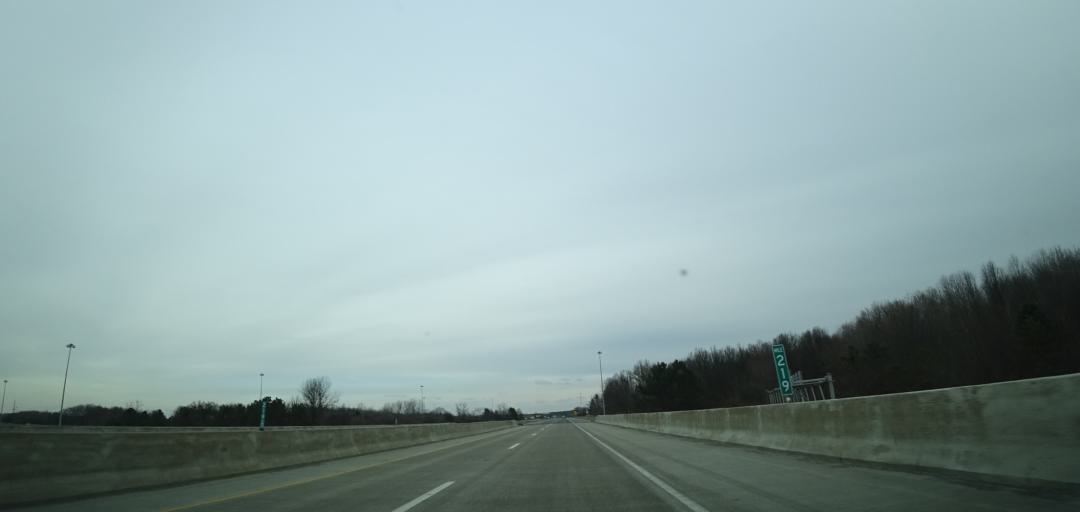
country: US
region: Ohio
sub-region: Trumbull County
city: Lordstown
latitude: 41.1102
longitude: -80.8383
